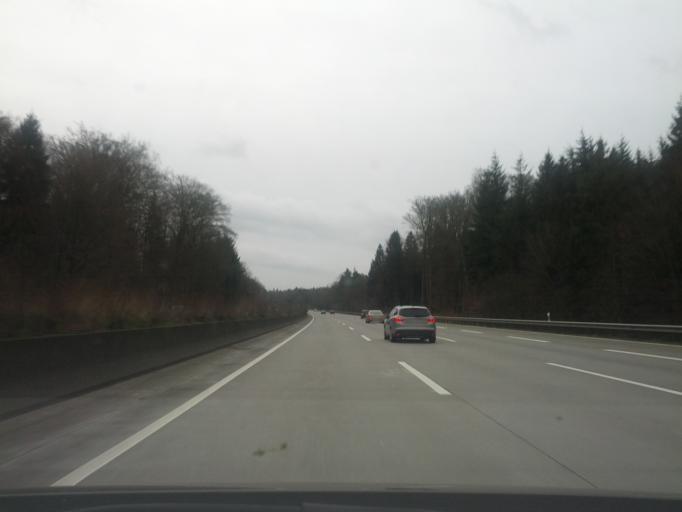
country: DE
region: Lower Saxony
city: Garlstorf
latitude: 53.2245
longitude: 10.0757
